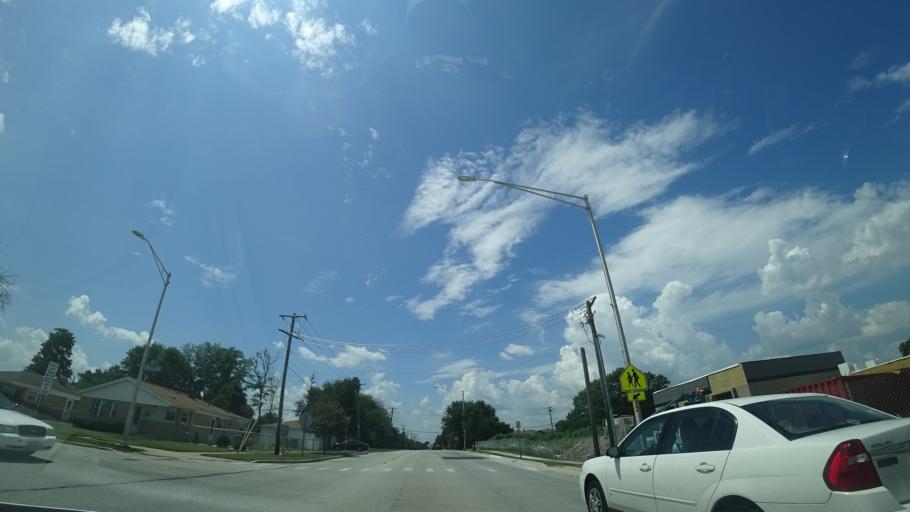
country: US
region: Illinois
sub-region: Cook County
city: Alsip
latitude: 41.6691
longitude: -87.7332
